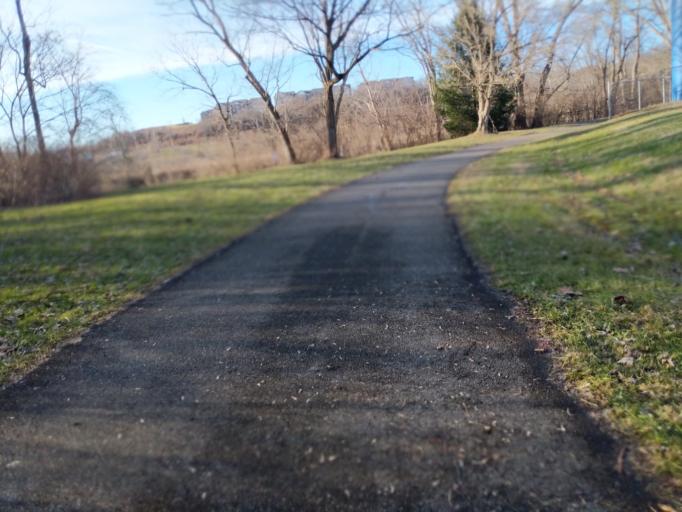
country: US
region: Ohio
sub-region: Athens County
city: Athens
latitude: 39.3326
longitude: -82.1254
